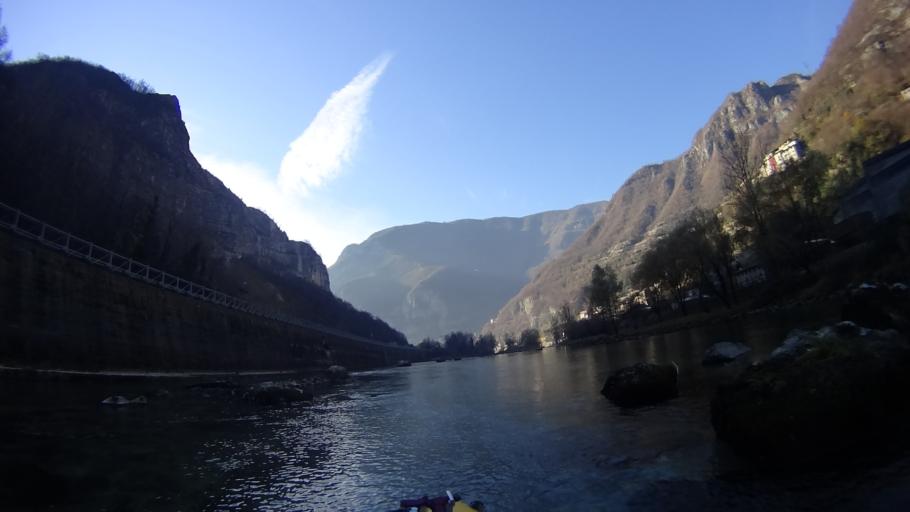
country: IT
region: Veneto
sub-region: Provincia di Vicenza
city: Valstagna
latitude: 45.8675
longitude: 11.6662
